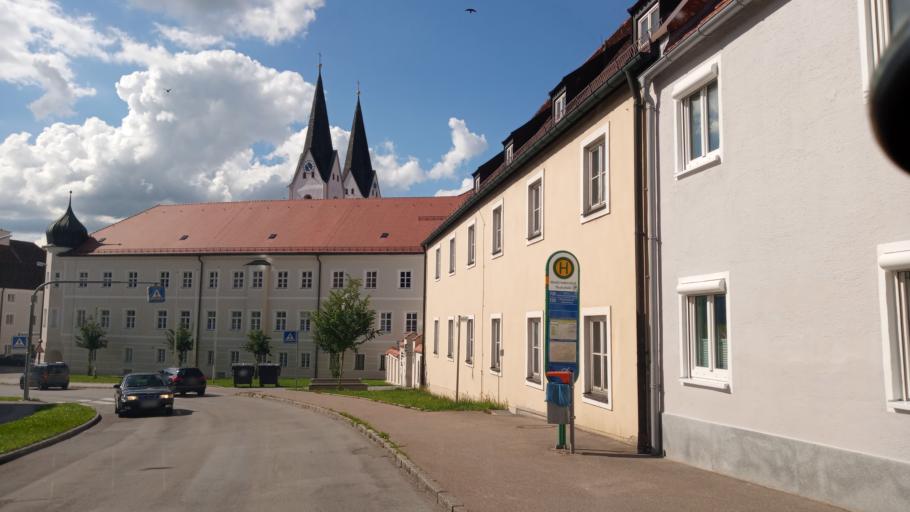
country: DE
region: Bavaria
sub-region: Upper Bavaria
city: Markt Indersdorf
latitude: 48.3563
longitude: 11.3840
